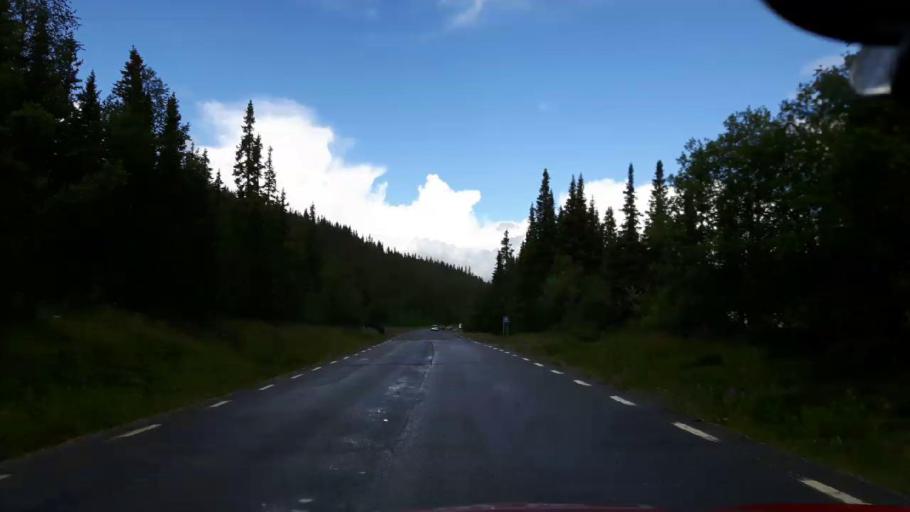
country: SE
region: Vaesterbotten
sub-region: Vilhelmina Kommun
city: Sjoberg
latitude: 65.0221
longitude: 15.1595
